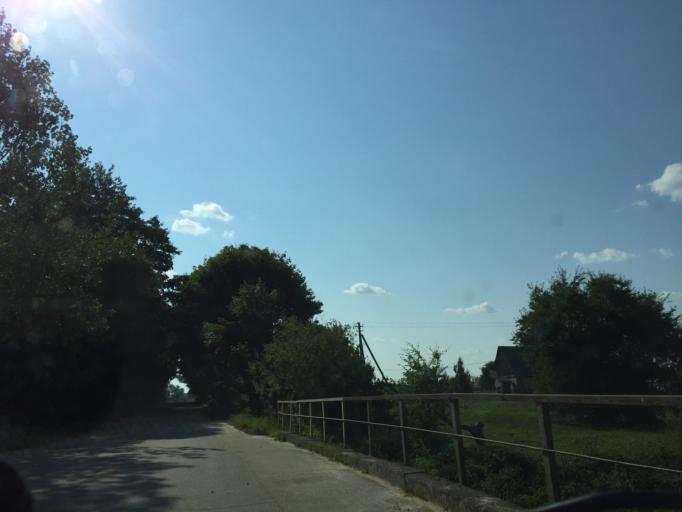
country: LV
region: Jelgava
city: Jelgava
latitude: 56.4561
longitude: 23.7018
